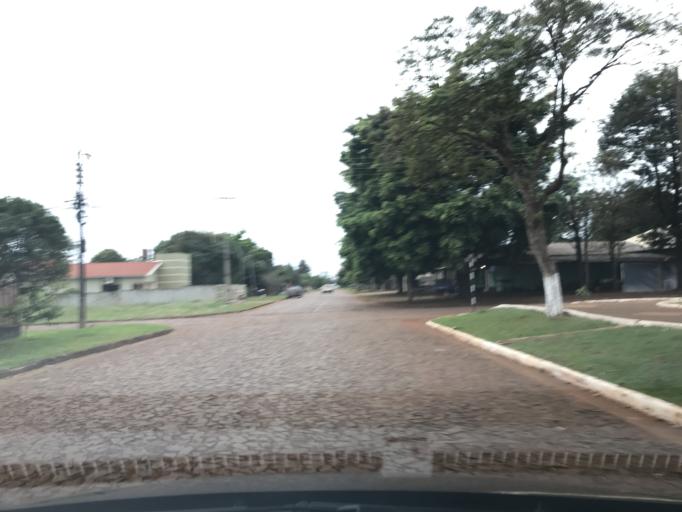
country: PY
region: Canindeyu
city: Colonia Catuete
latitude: -24.2481
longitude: -54.7597
